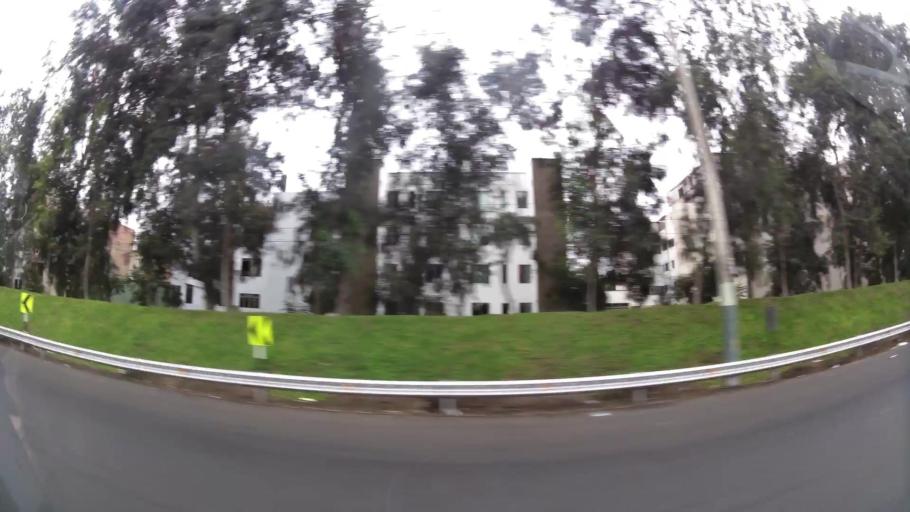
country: PE
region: Lima
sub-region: Lima
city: San Luis
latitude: -12.0922
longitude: -76.9809
